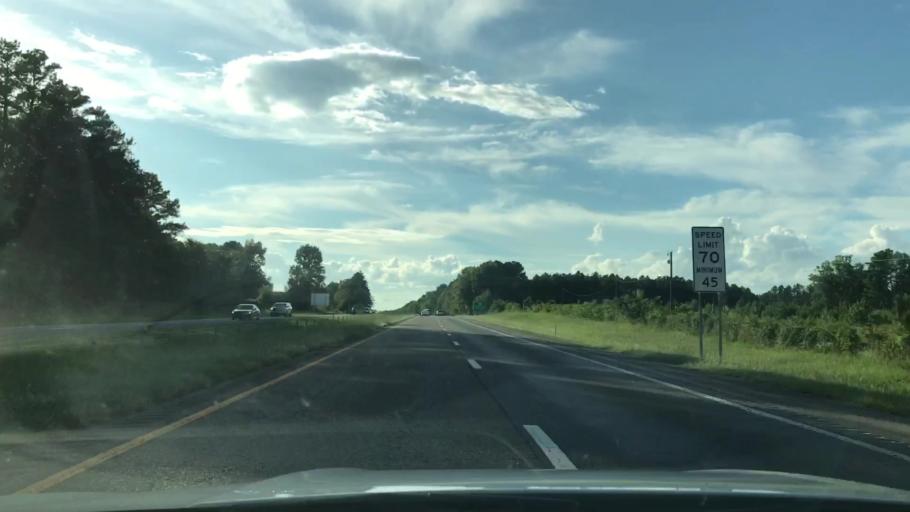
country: US
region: South Carolina
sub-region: Newberry County
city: Newberry
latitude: 34.3000
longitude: -81.5554
